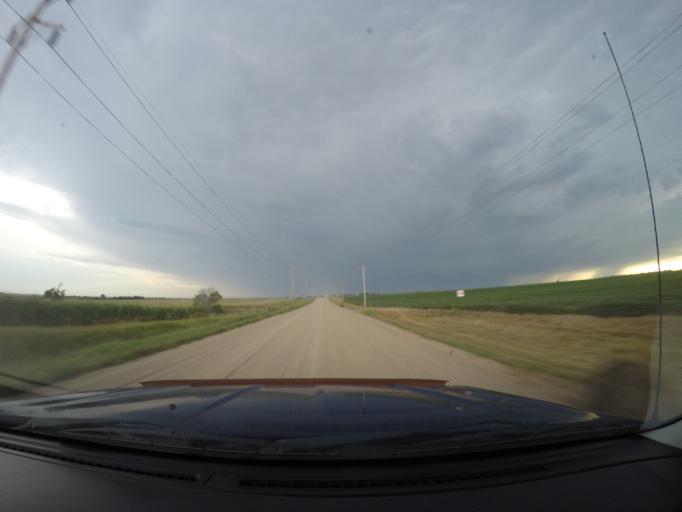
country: US
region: Nebraska
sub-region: Buffalo County
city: Kearney
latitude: 40.8440
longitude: -99.2306
